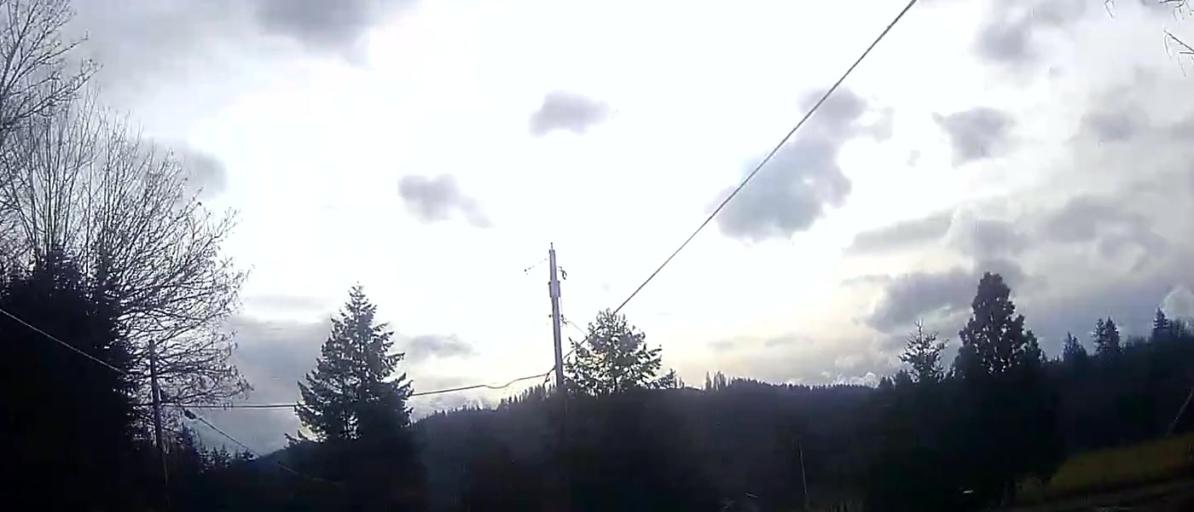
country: US
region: Washington
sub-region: Skagit County
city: Sedro-Woolley
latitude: 48.5678
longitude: -122.2978
